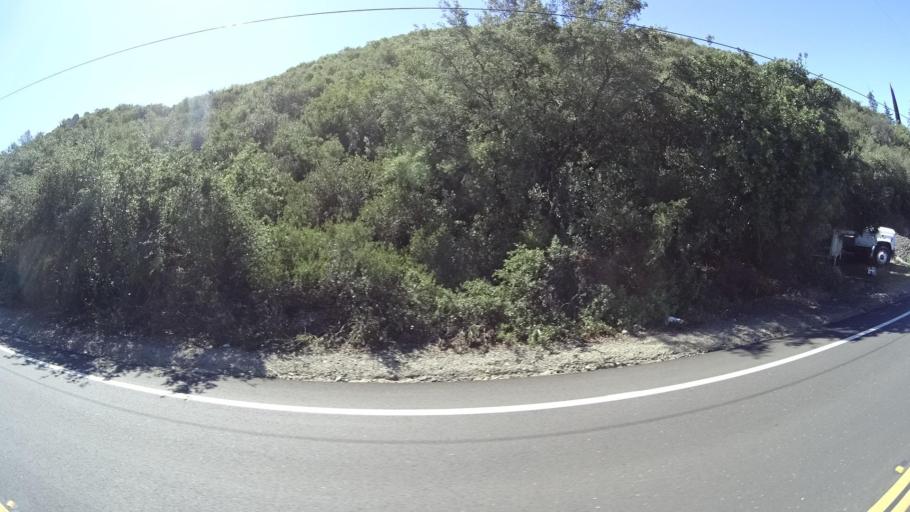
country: US
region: California
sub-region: San Diego County
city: Jamul
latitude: 32.7344
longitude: -116.8020
